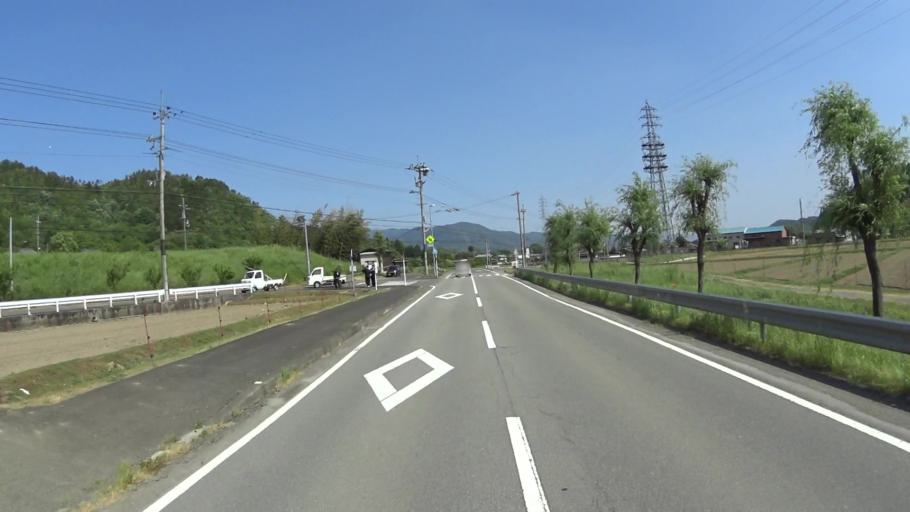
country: JP
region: Kyoto
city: Kameoka
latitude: 35.1072
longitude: 135.5235
